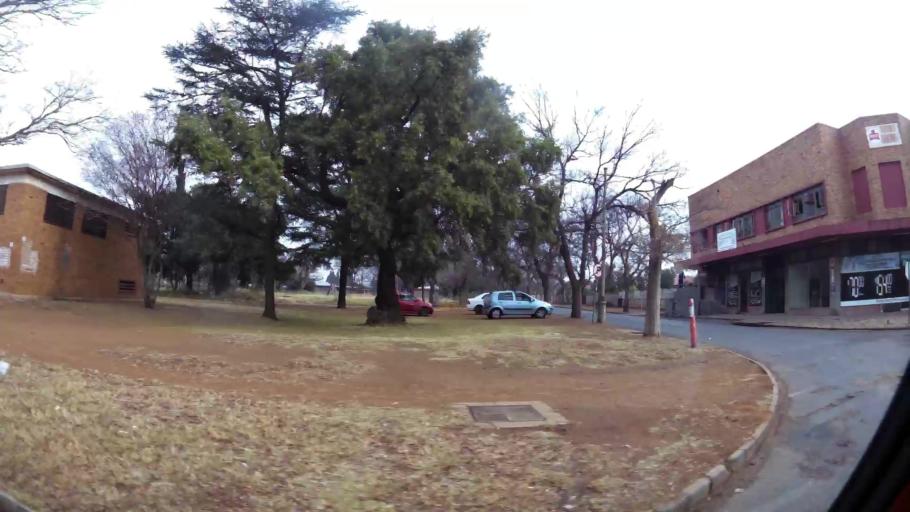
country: ZA
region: Gauteng
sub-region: Sedibeng District Municipality
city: Vanderbijlpark
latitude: -26.6923
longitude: 27.8195
